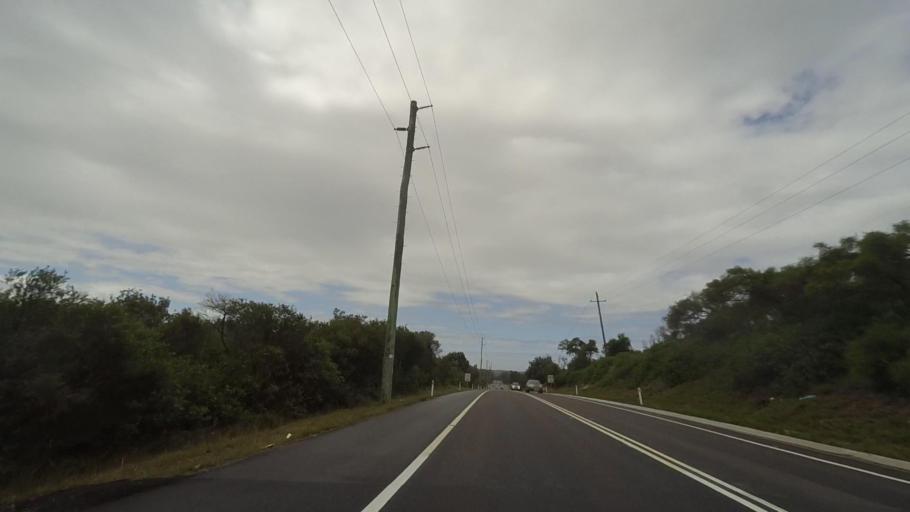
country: AU
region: New South Wales
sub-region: Wyong Shire
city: The Entrance
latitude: -33.3229
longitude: 151.5138
